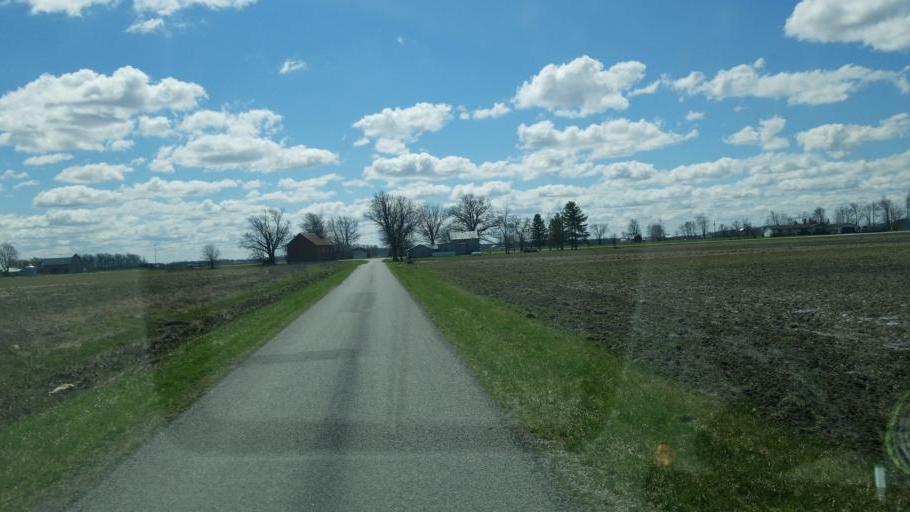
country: US
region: Ohio
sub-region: Hancock County
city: Findlay
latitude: 41.0149
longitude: -83.5110
